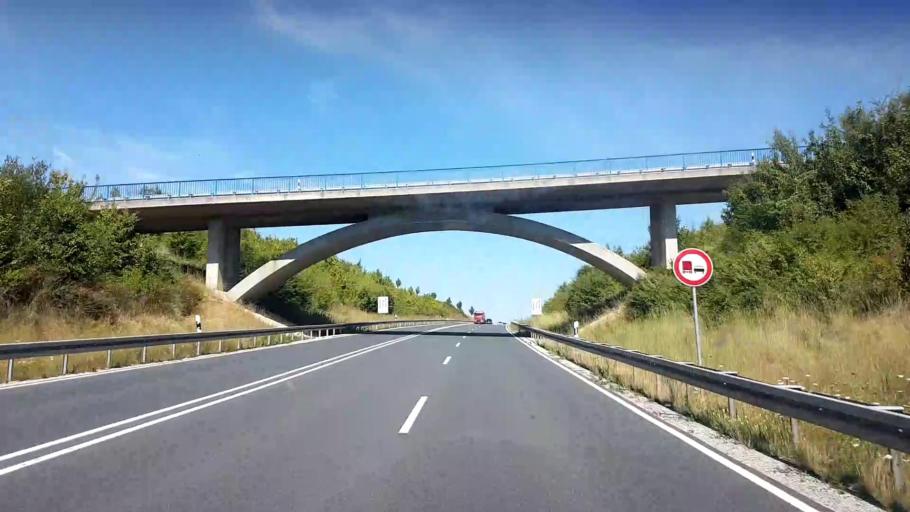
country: DE
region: Bavaria
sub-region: Upper Franconia
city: Untersiemau
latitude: 50.1682
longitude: 10.9948
